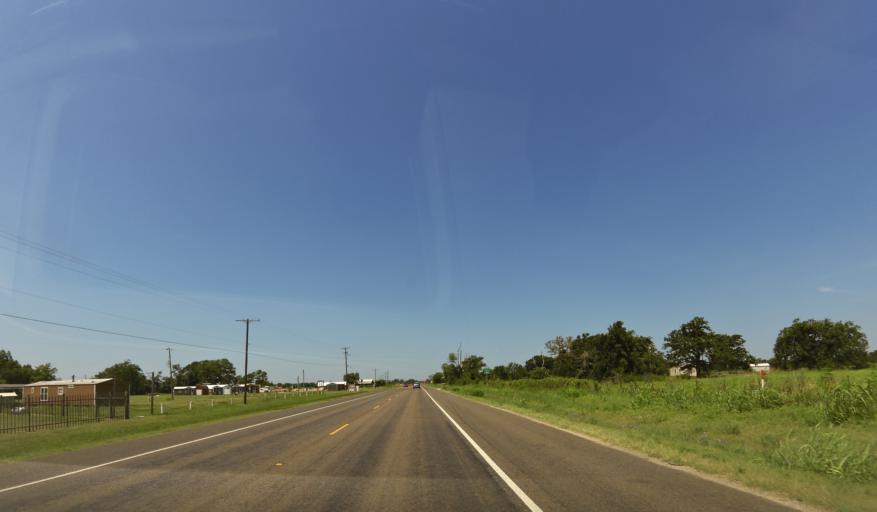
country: US
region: Texas
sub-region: Grimes County
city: Navasota
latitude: 30.3717
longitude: -96.1284
